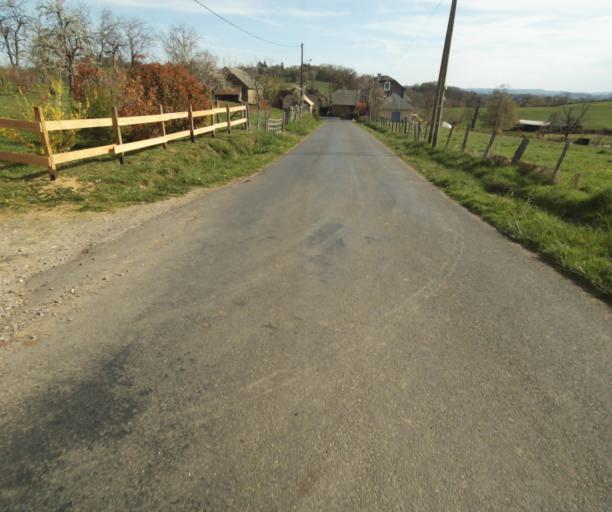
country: FR
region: Limousin
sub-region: Departement de la Correze
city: Naves
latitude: 45.3301
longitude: 1.7331
